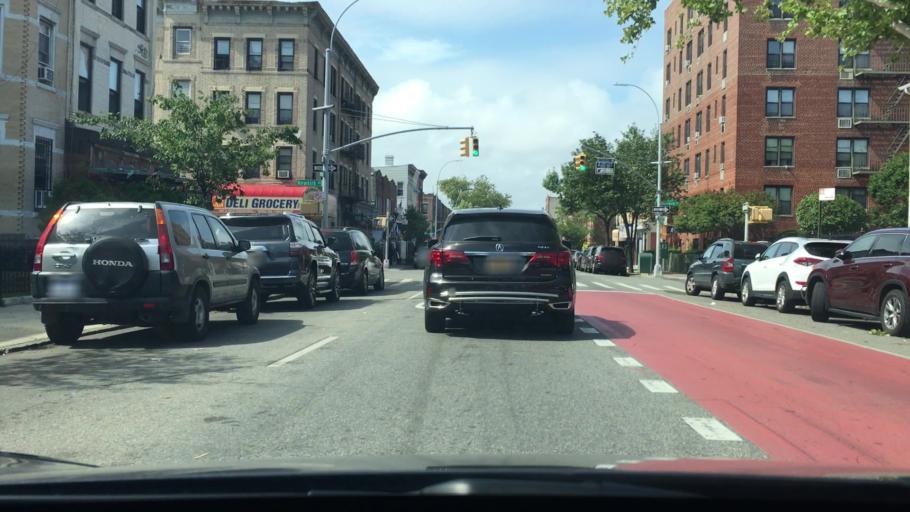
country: US
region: New York
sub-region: Kings County
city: Brooklyn
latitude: 40.6395
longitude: -73.9513
